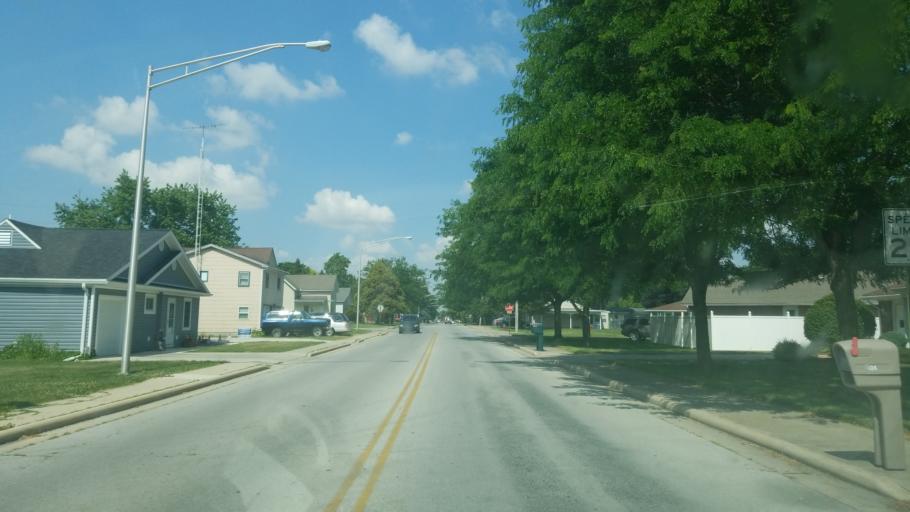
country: US
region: Ohio
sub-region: Auglaize County
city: Wapakoneta
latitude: 40.5700
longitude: -84.1789
